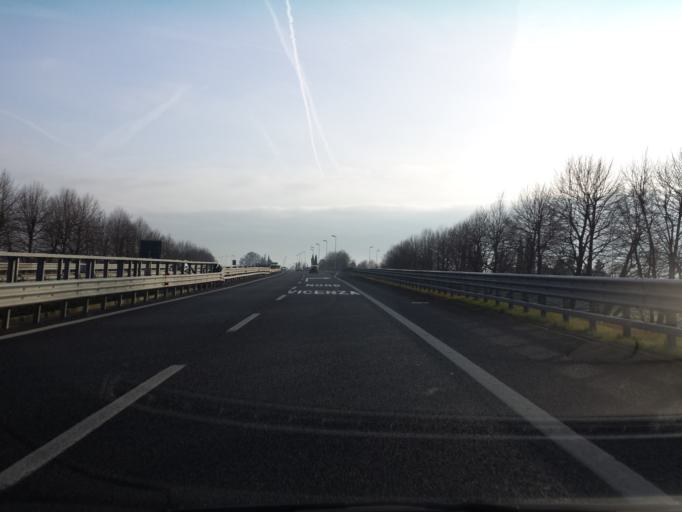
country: IT
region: Veneto
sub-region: Provincia di Vicenza
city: Lisiera
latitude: 45.5836
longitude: 11.5992
